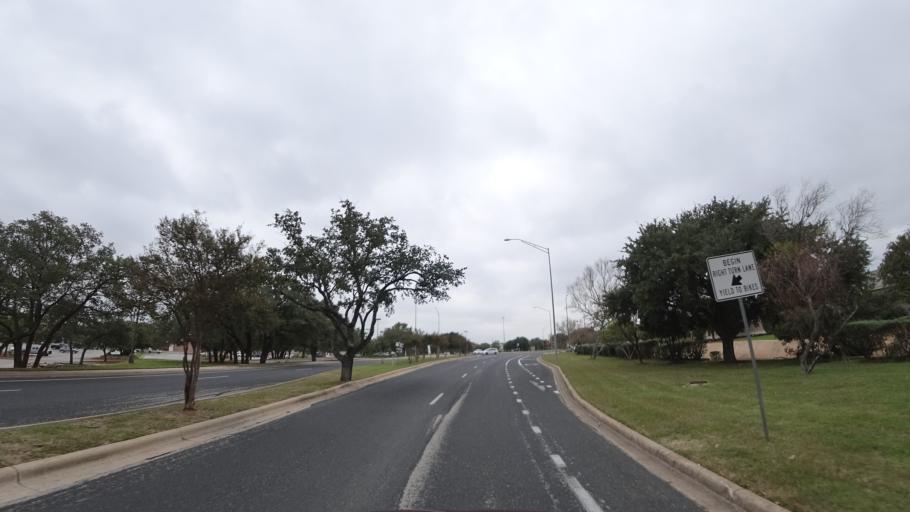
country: US
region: Texas
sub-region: Williamson County
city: Anderson Mill
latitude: 30.4705
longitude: -97.8022
